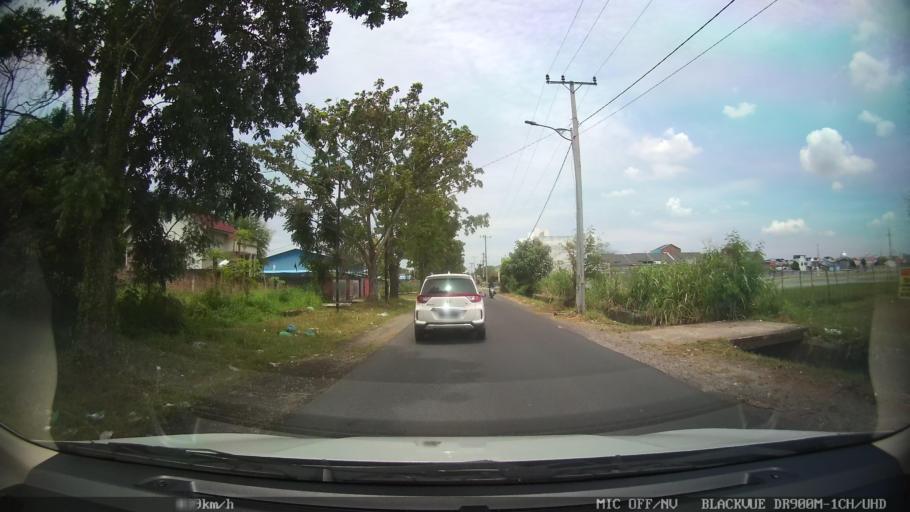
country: ID
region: North Sumatra
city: Medan
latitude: 3.5551
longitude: 98.6448
